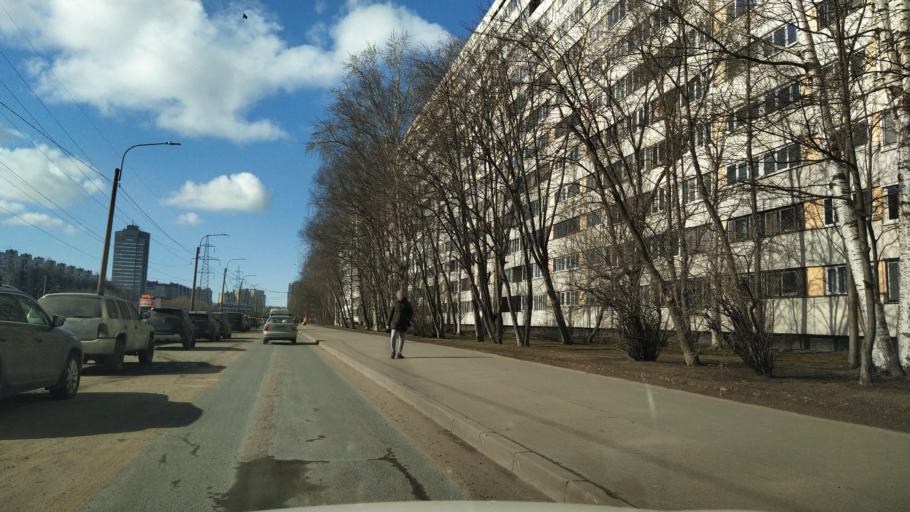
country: RU
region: St.-Petersburg
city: Komendantsky aerodrom
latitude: 60.0051
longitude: 30.2869
